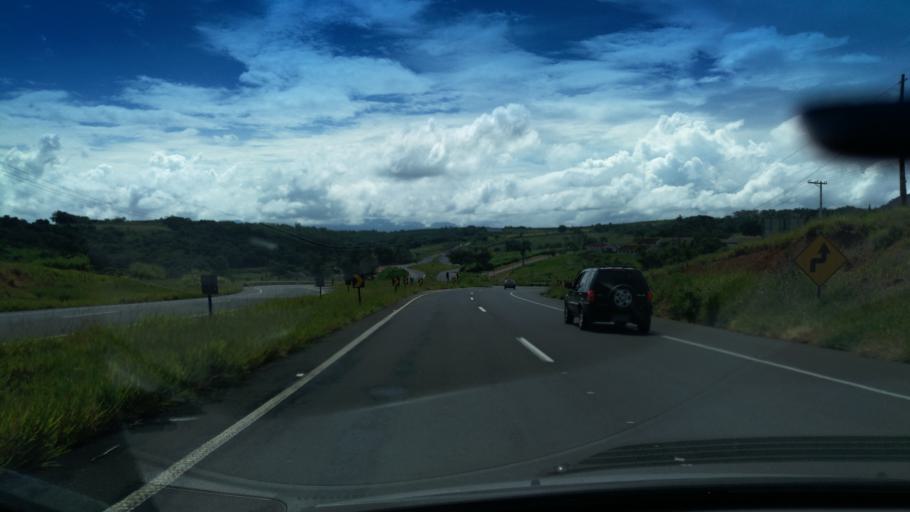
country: BR
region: Sao Paulo
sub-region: Santo Antonio Do Jardim
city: Espirito Santo do Pinhal
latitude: -22.1685
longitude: -46.7407
